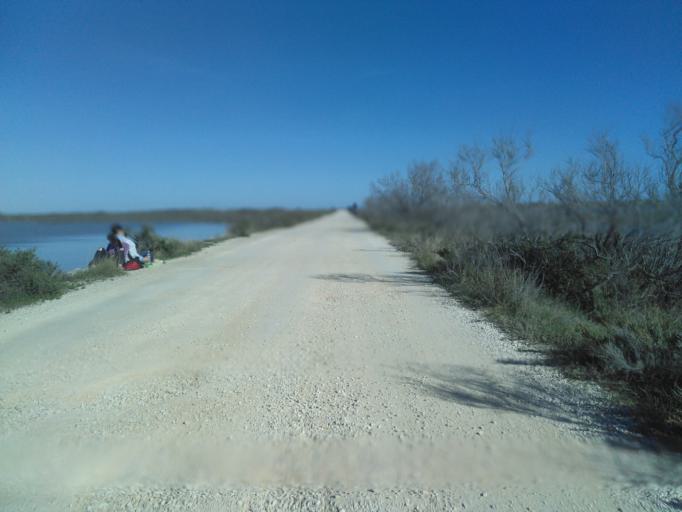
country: FR
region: Provence-Alpes-Cote d'Azur
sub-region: Departement des Bouches-du-Rhone
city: Saintes-Maries-de-la-Mer
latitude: 43.4614
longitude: 4.4843
